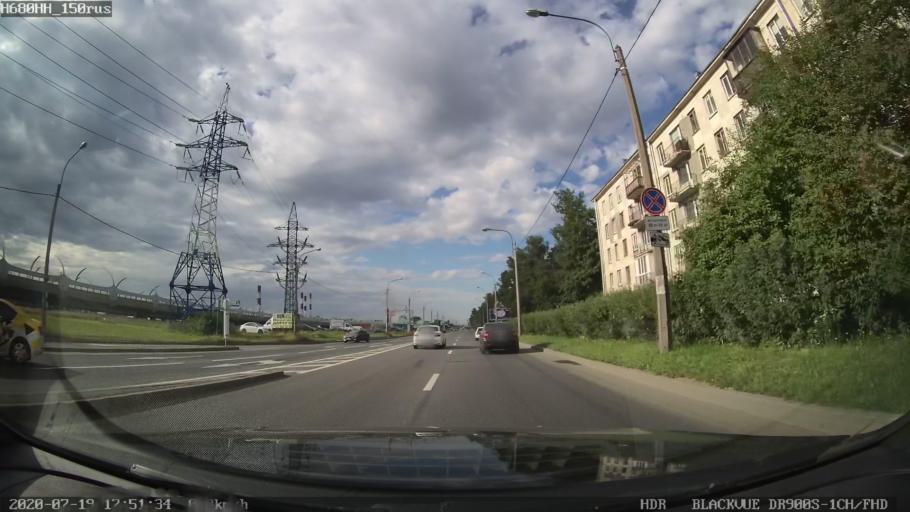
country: RU
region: St.-Petersburg
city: Avtovo
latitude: 59.8583
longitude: 30.2942
